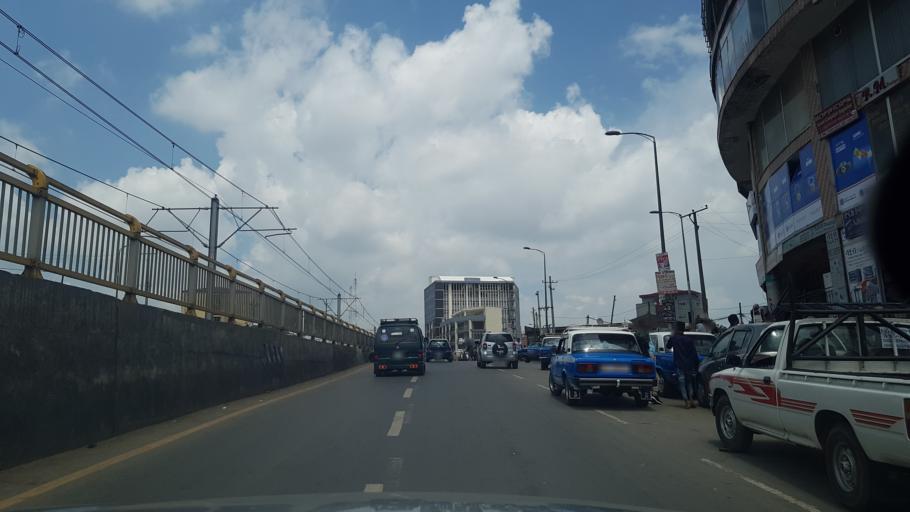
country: ET
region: Adis Abeba
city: Addis Ababa
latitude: 9.0344
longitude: 38.7455
